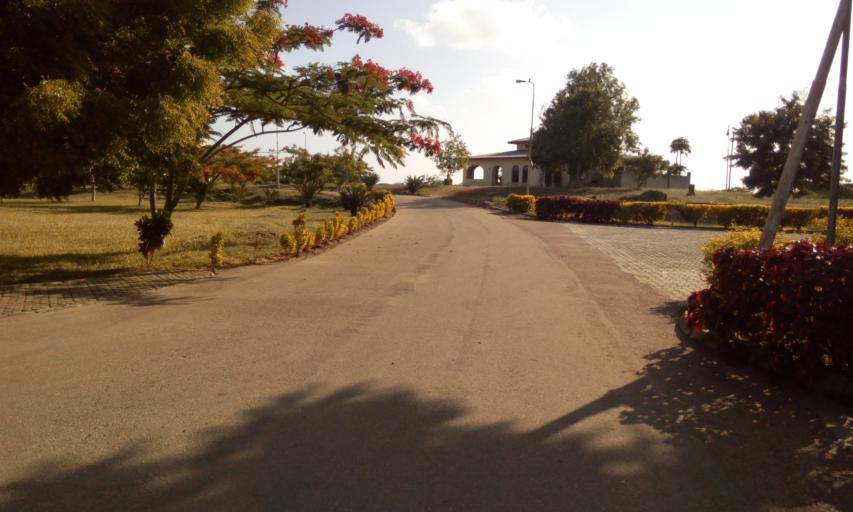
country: TZ
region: Zanzibar Central/South
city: Koani
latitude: -6.1991
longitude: 39.3063
